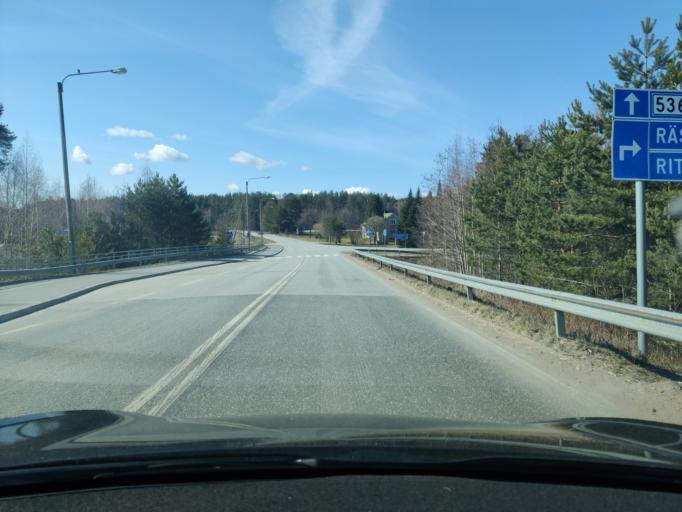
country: FI
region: Northern Savo
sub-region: Kuopio
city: Vehmersalmi
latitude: 62.7679
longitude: 27.9997
